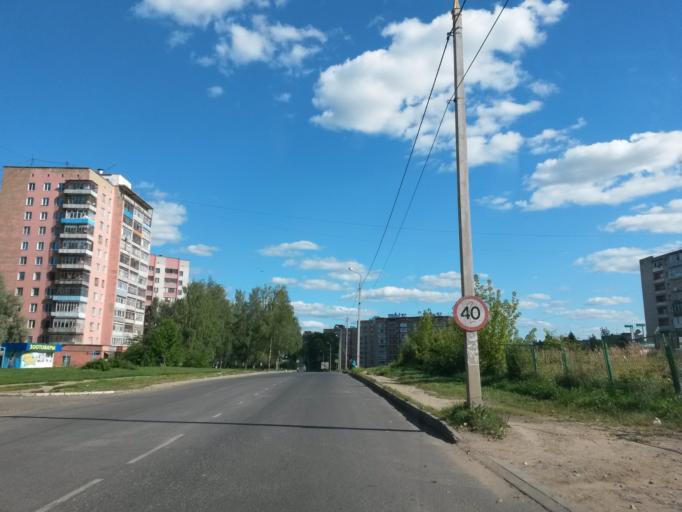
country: RU
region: Jaroslavl
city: Yaroslavl
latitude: 57.5796
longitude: 39.8580
